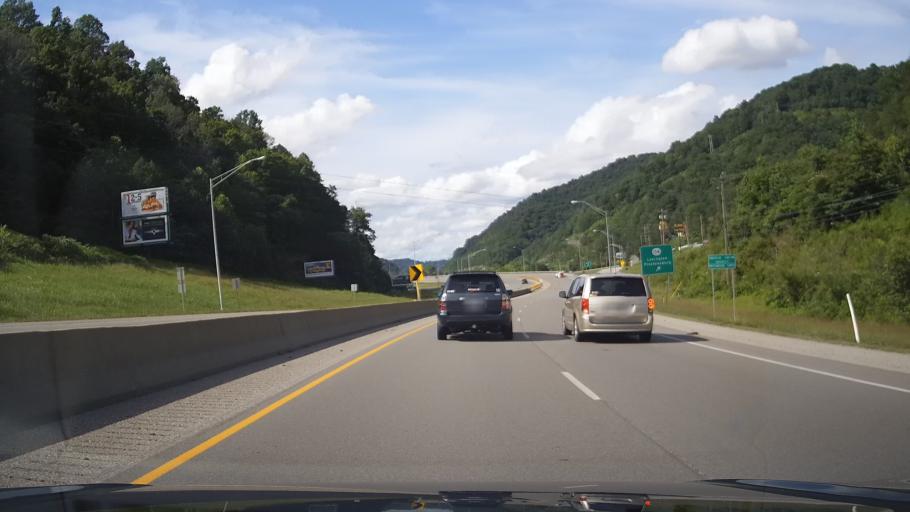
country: US
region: Kentucky
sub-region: Floyd County
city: Prestonsburg
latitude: 37.6529
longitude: -82.7855
